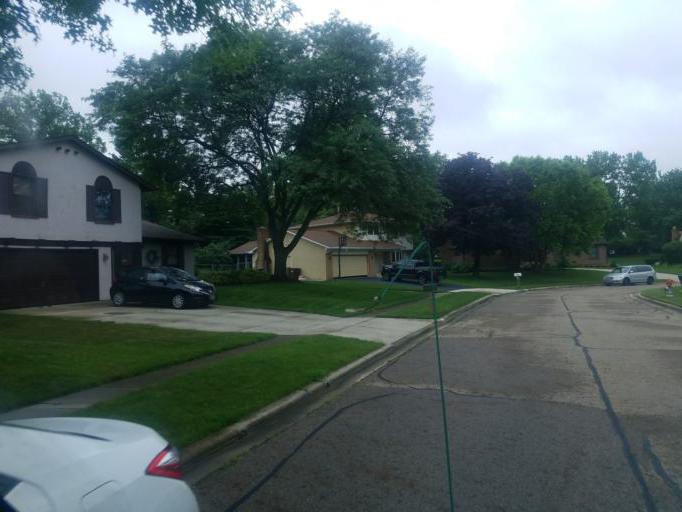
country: US
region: Ohio
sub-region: Franklin County
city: Gahanna
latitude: 40.0168
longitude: -82.8556
